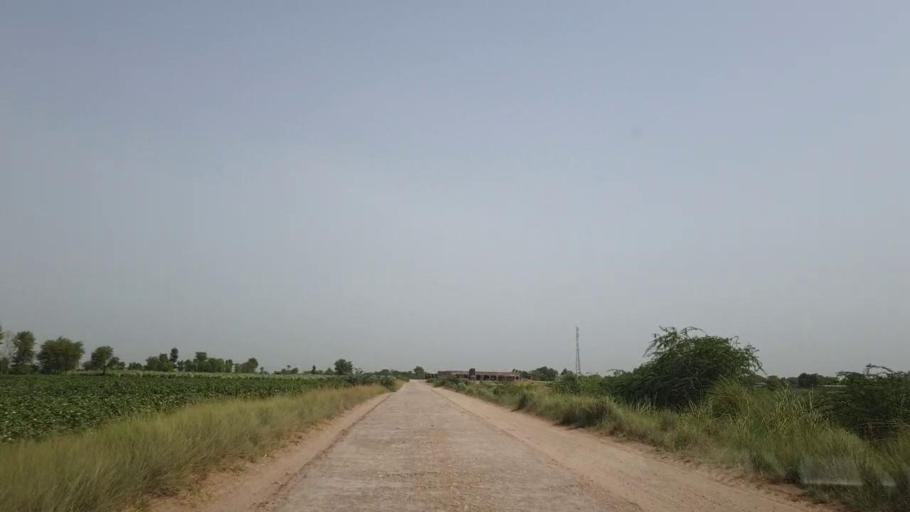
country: PK
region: Sindh
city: Sakrand
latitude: 26.1386
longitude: 68.3642
